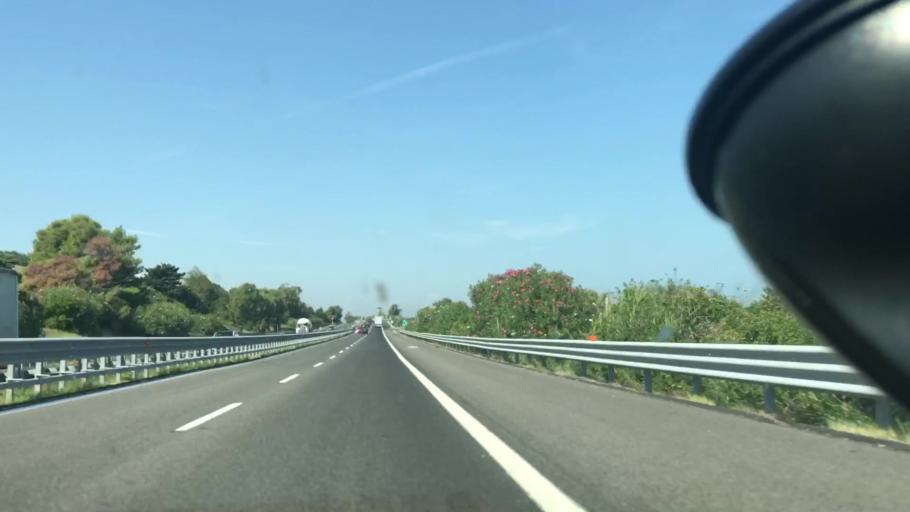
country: IT
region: Molise
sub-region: Provincia di Campobasso
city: Petacciato
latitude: 42.0264
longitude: 14.8780
